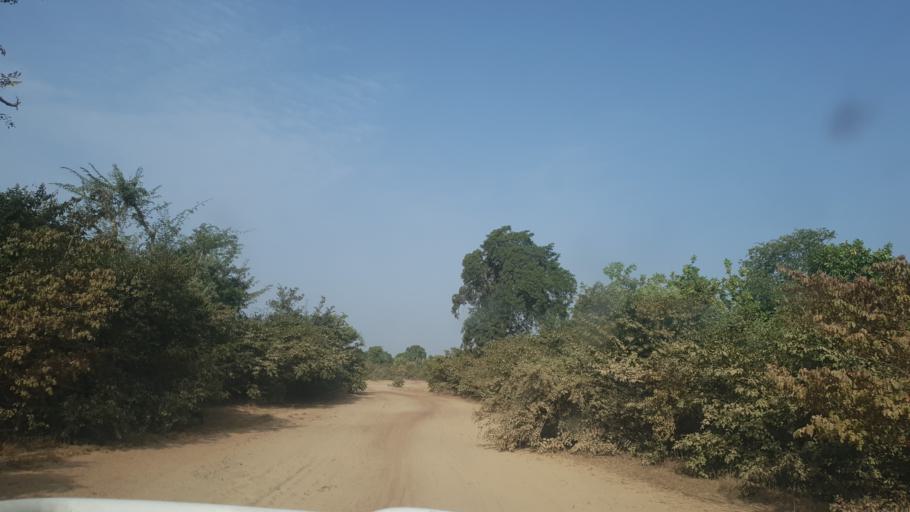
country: ML
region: Segou
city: Baroueli
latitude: 13.3636
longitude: -6.9200
